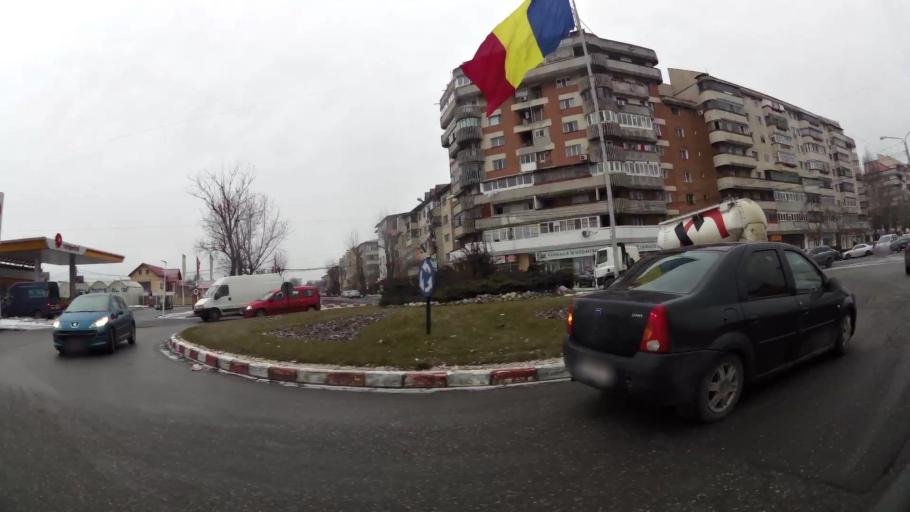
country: RO
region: Dambovita
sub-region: Comuna Ulmi
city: Ulmi
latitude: 44.9155
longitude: 25.4822
